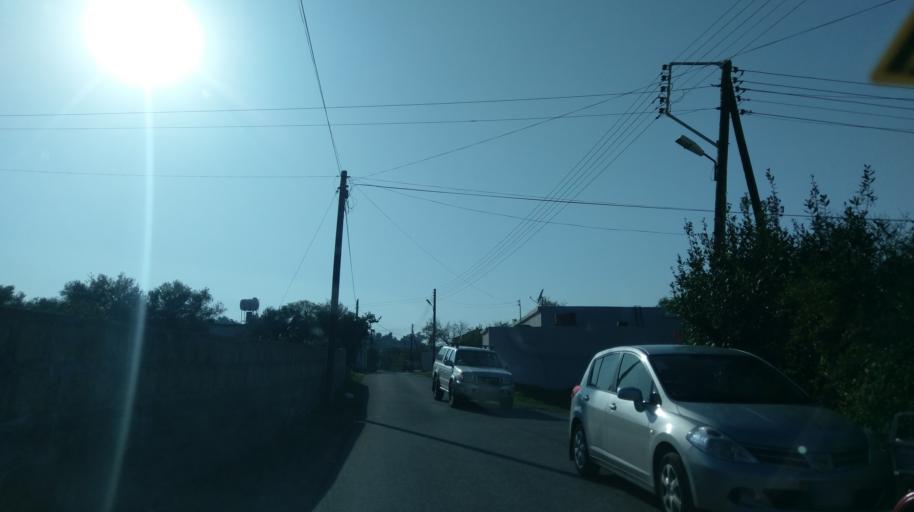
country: CY
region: Ammochostos
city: Leonarisso
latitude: 35.5403
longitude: 34.1937
